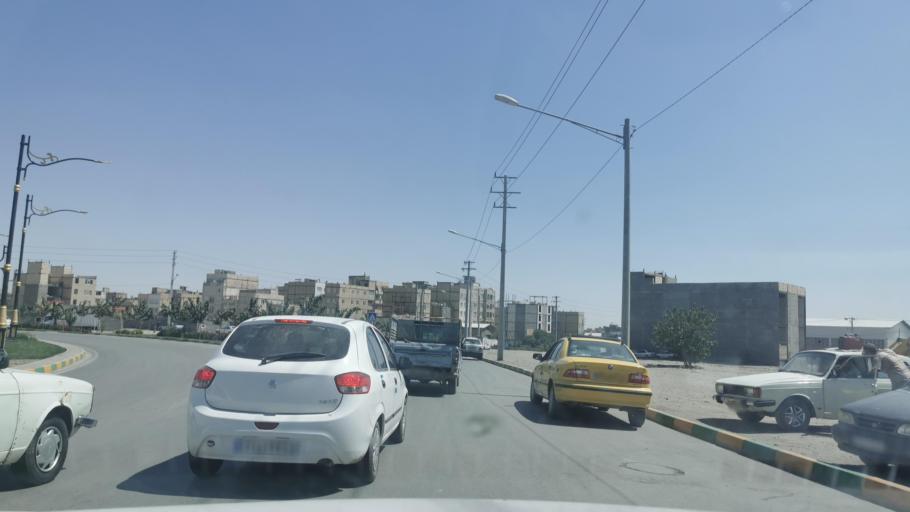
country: IR
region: Razavi Khorasan
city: Mashhad
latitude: 36.3529
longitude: 59.5706
